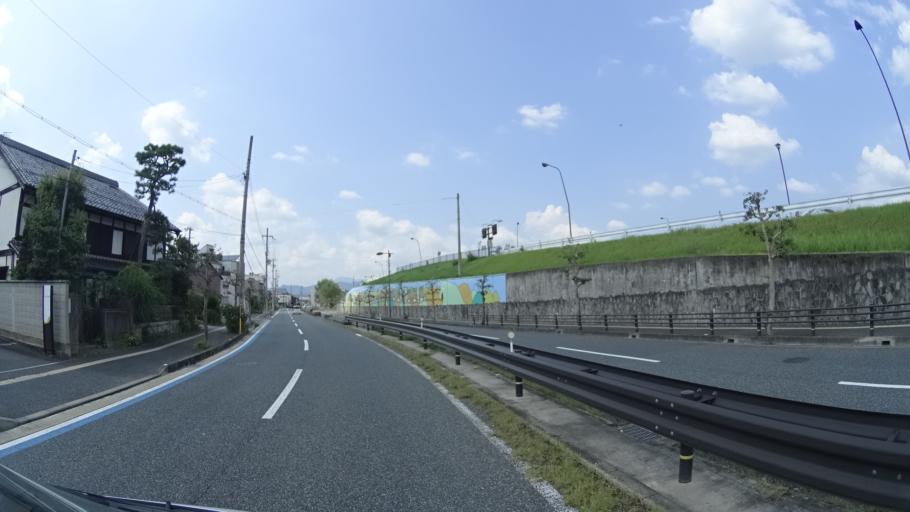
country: JP
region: Kyoto
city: Fukuchiyama
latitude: 35.3007
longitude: 135.1279
